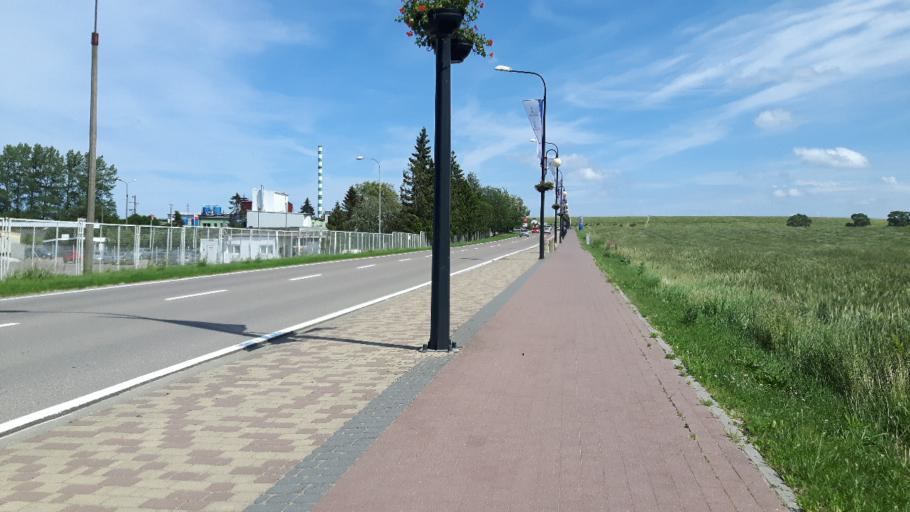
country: PL
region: Pomeranian Voivodeship
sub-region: Powiat wejherowski
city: Gniewino
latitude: 54.7153
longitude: 18.0372
